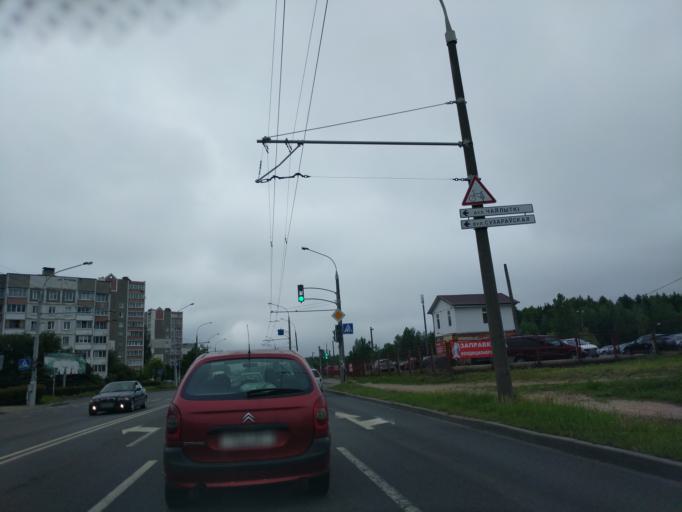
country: BY
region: Minsk
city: Novoye Medvezhino
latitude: 53.8887
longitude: 27.4426
